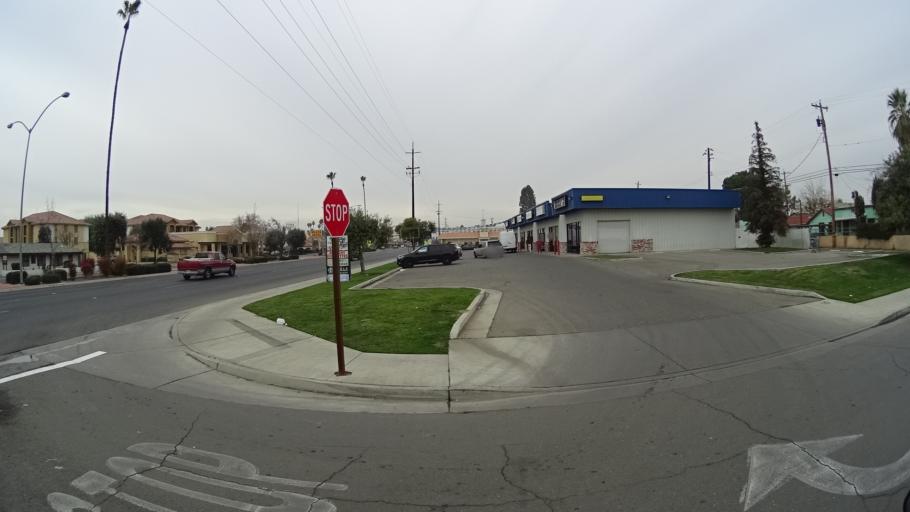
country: US
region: California
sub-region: Kern County
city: Bakersfield
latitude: 35.3626
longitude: -119.0026
